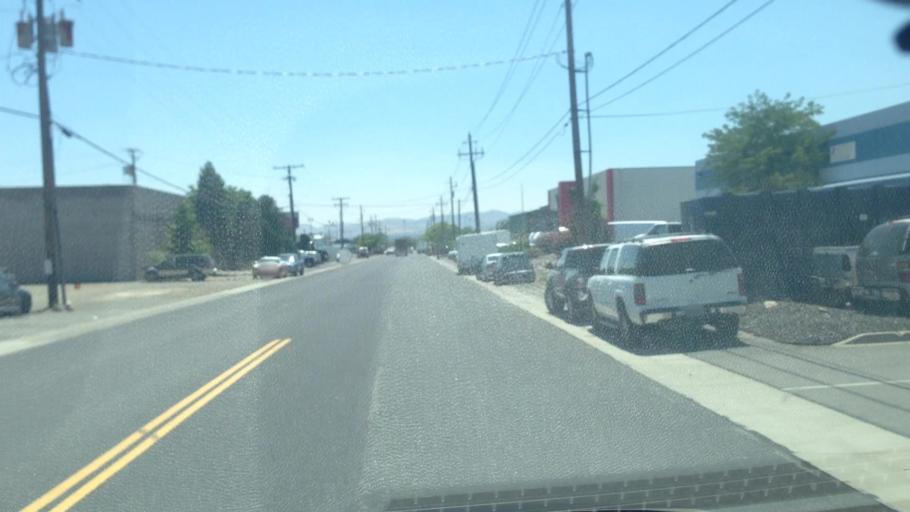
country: US
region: Nevada
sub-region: Washoe County
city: Sparks
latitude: 39.5168
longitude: -119.7735
